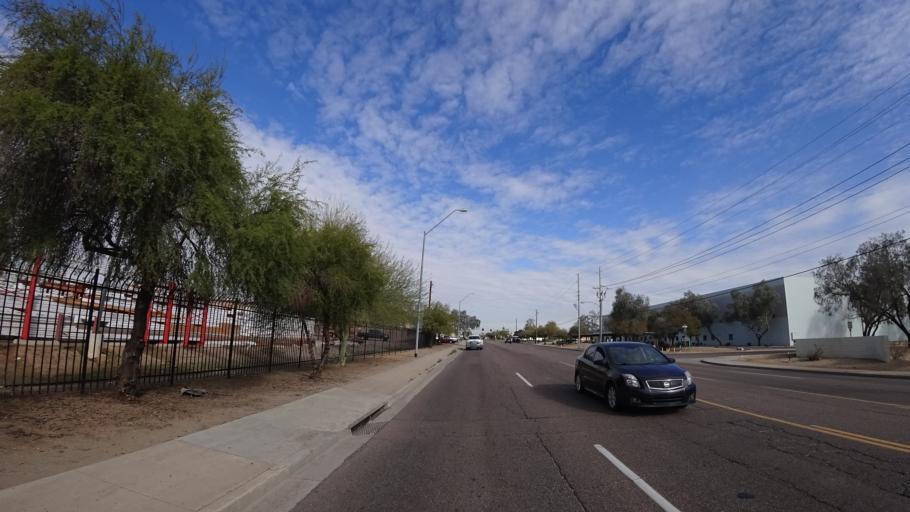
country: US
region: Arizona
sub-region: Maricopa County
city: Phoenix
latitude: 33.4495
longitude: -112.1519
